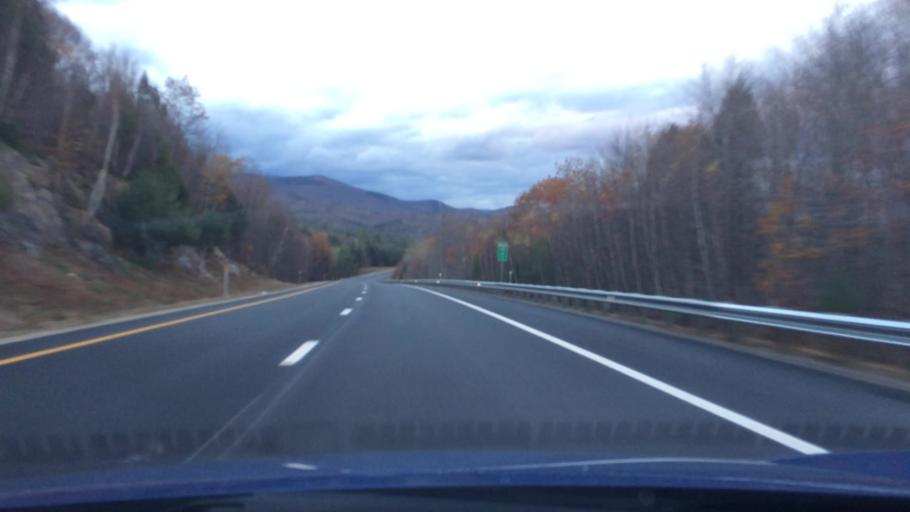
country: US
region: New Hampshire
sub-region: Grafton County
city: Thornton
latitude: 43.9039
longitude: -71.6890
